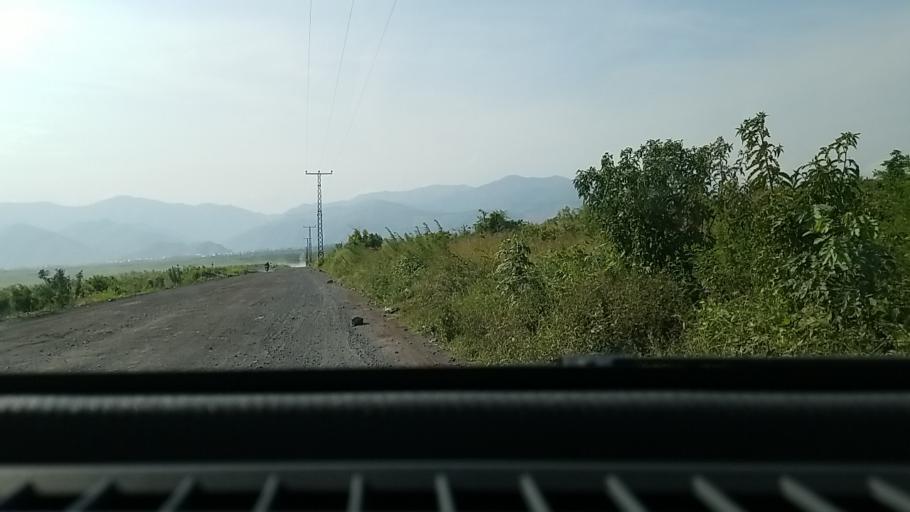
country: CD
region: Nord Kivu
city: Sake
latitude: -1.5885
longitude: 29.0931
